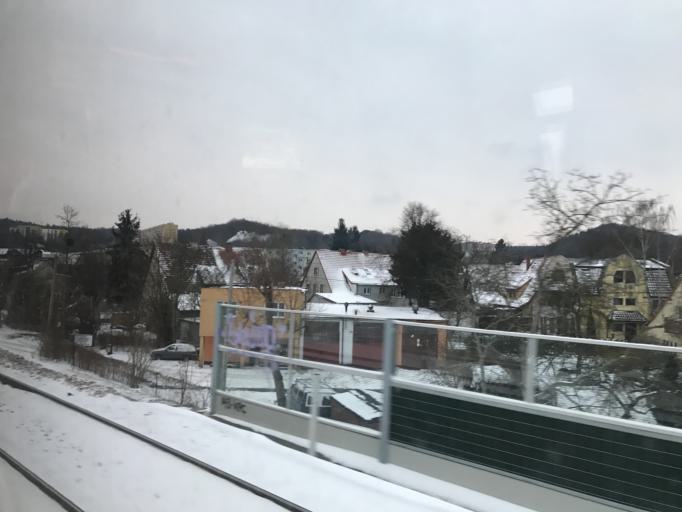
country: PL
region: Pomeranian Voivodeship
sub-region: Sopot
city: Sopot
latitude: 54.3900
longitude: 18.5764
